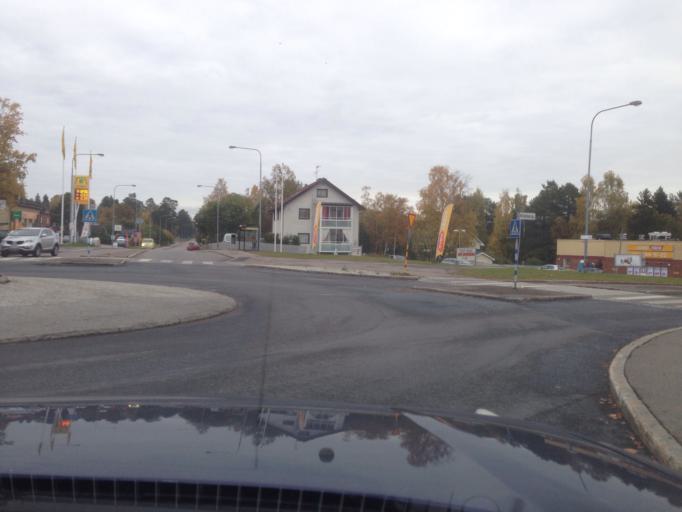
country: SE
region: Vaesternorrland
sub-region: Sundsvalls Kommun
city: Sundsvall
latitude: 62.4007
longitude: 17.3277
